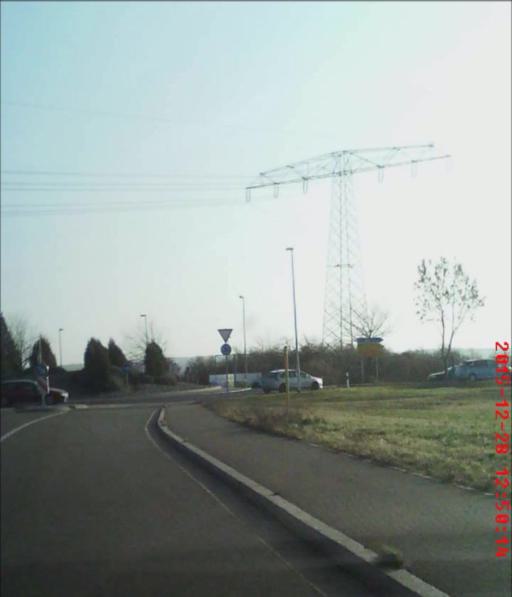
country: DE
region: Thuringia
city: Niederrossla
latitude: 51.0148
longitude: 11.4696
